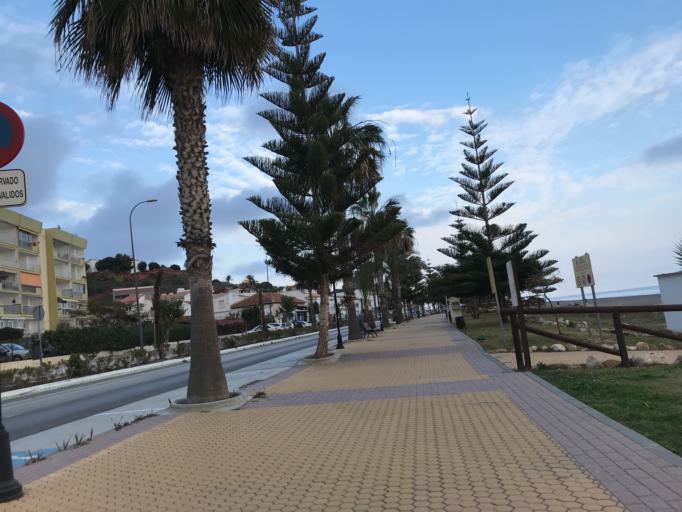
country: ES
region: Andalusia
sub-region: Provincia de Malaga
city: Valdes
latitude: 36.7160
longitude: -4.1915
